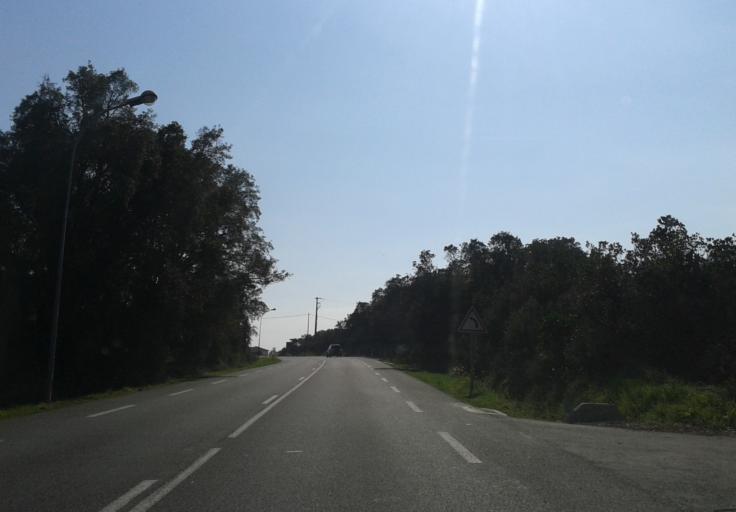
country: FR
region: Corsica
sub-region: Departement de la Haute-Corse
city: Linguizzetta
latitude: 42.2170
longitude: 9.5344
